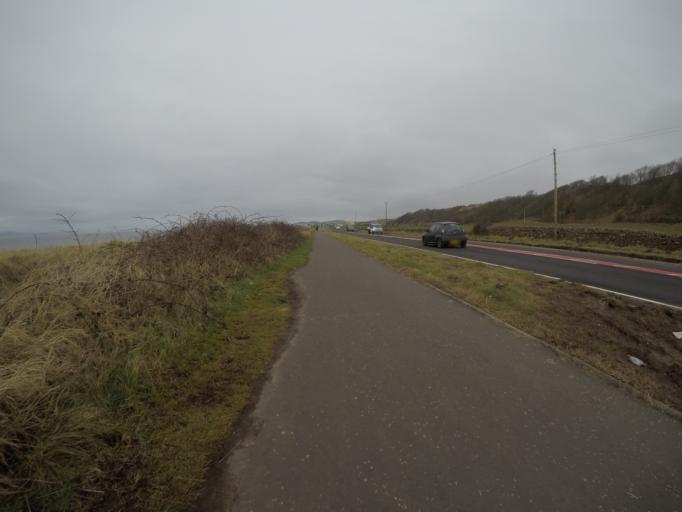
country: GB
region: Scotland
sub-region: North Ayrshire
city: West Kilbride
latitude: 55.6698
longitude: -4.8452
